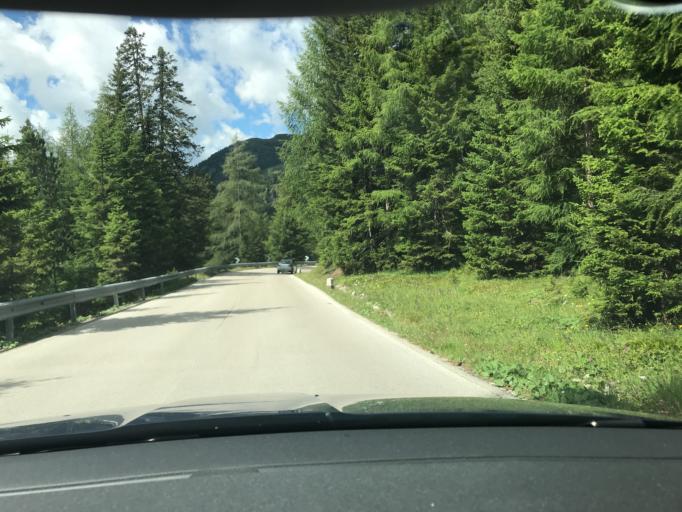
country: IT
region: Veneto
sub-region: Provincia di Belluno
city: Livinallongo del Col di Lana
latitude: 46.5106
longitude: 11.9968
